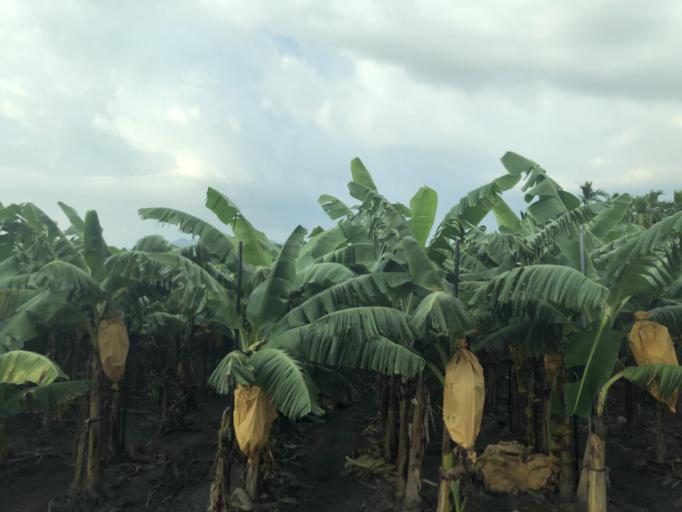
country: TW
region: Taiwan
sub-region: Pingtung
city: Pingtung
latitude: 22.8663
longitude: 120.5405
